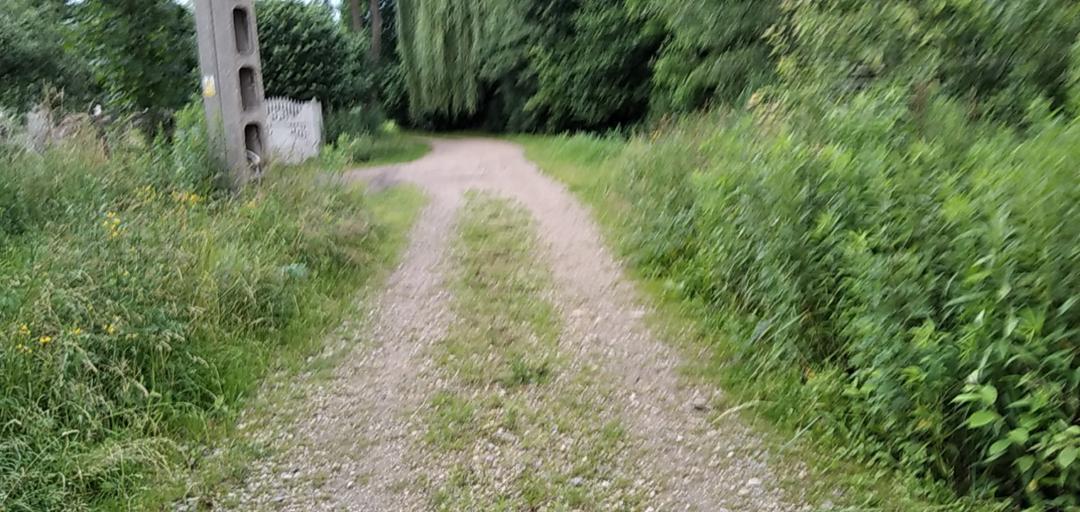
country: PL
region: Silesian Voivodeship
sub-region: Powiat bedzinski
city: Psary
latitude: 50.4001
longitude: 19.1281
